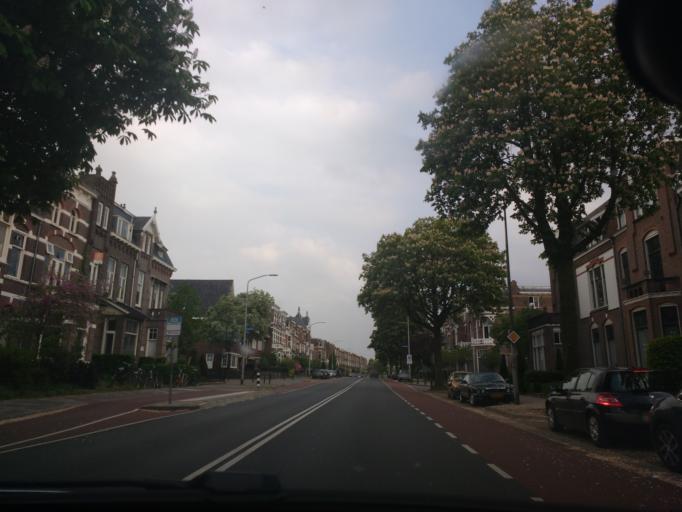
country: NL
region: Gelderland
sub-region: Gemeente Nijmegen
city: Nijmegen
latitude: 51.8391
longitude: 5.8642
